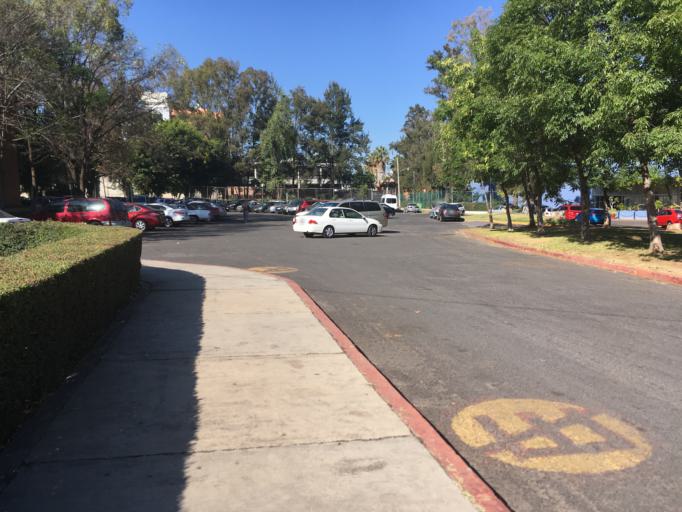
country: MX
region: Michoacan
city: Morelia
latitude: 19.6829
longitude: -101.1828
